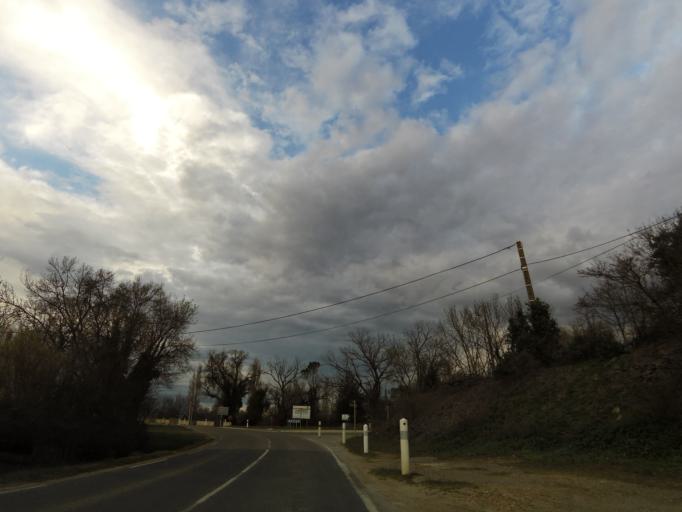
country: FR
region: Languedoc-Roussillon
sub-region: Departement du Gard
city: Vestric-et-Candiac
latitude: 43.7183
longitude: 4.2644
